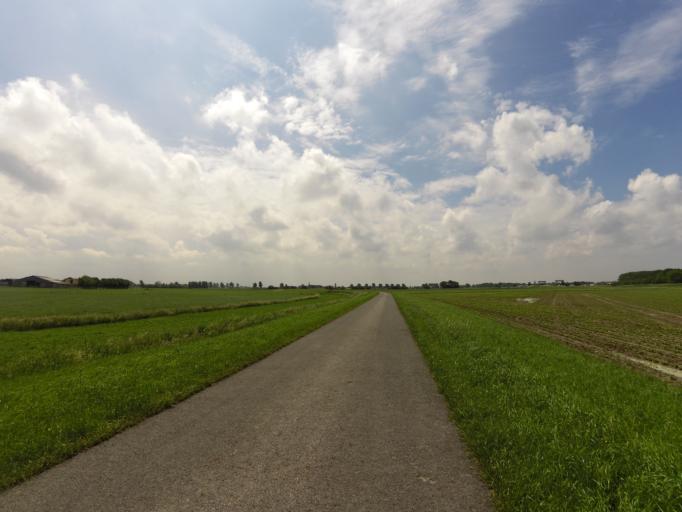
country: BE
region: Flanders
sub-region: Provincie West-Vlaanderen
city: Nieuwpoort
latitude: 51.1420
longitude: 2.7869
